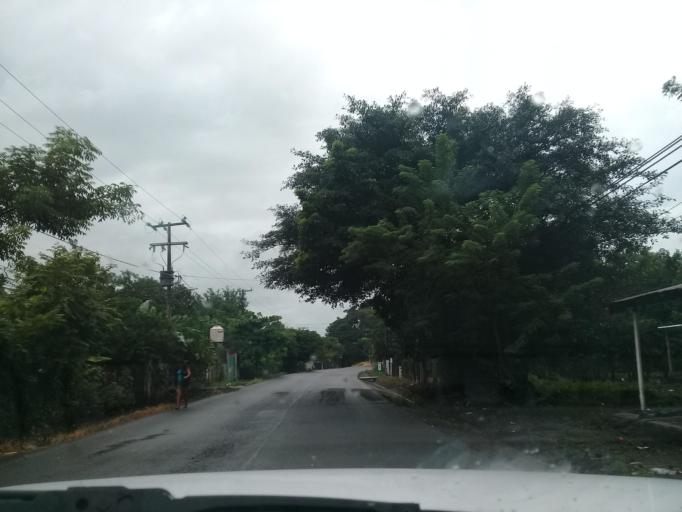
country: MX
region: Veracruz
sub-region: San Andres Tuxtla
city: Cerro las Iguanas
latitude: 18.4226
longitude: -95.2177
